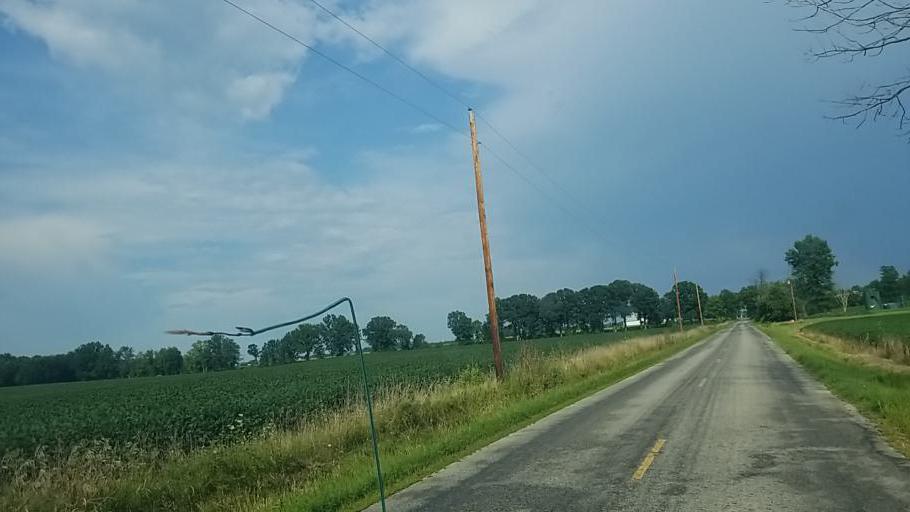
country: US
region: Ohio
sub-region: Wayne County
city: Creston
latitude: 40.9157
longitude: -81.9242
